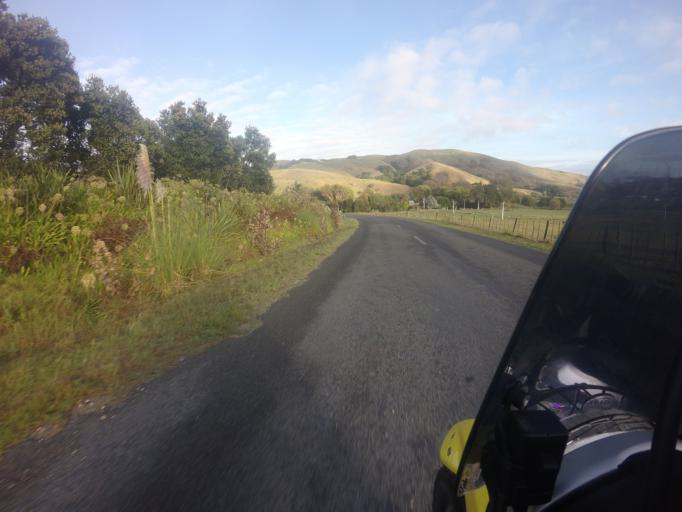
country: NZ
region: Gisborne
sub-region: Gisborne District
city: Gisborne
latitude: -38.6717
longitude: 178.0832
